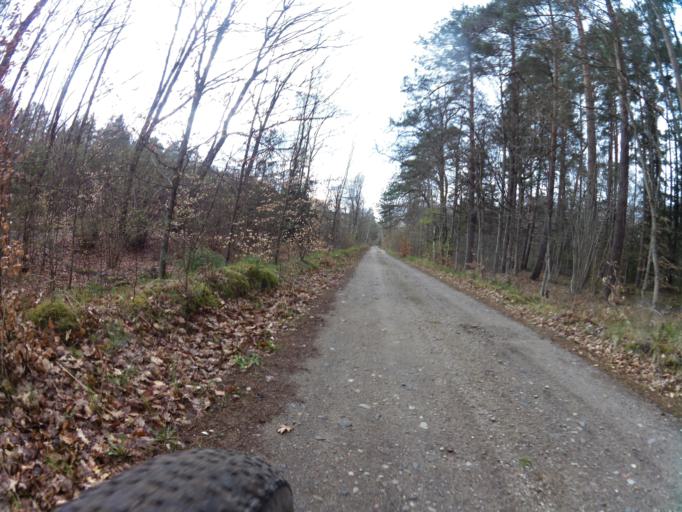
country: PL
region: West Pomeranian Voivodeship
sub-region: Powiat slawienski
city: Slawno
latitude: 54.3210
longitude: 16.7719
